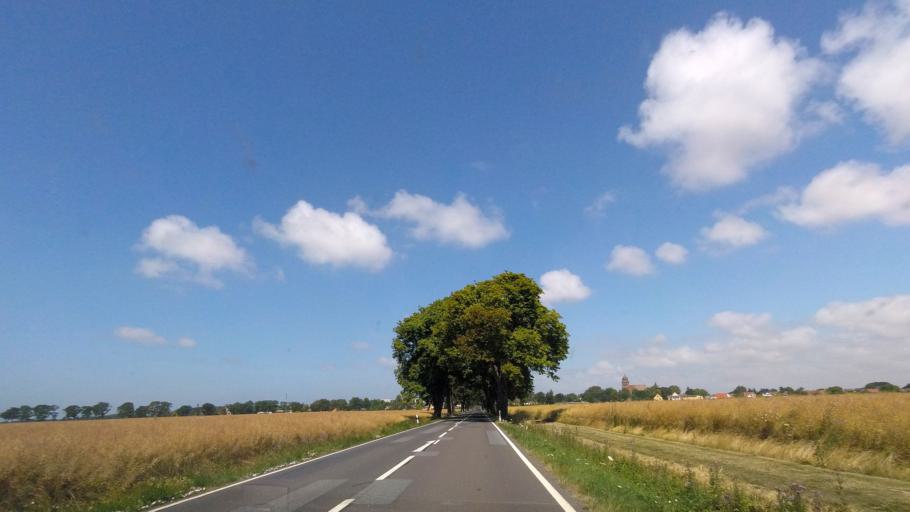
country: DE
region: Mecklenburg-Vorpommern
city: Gingst
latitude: 54.4499
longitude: 13.2608
